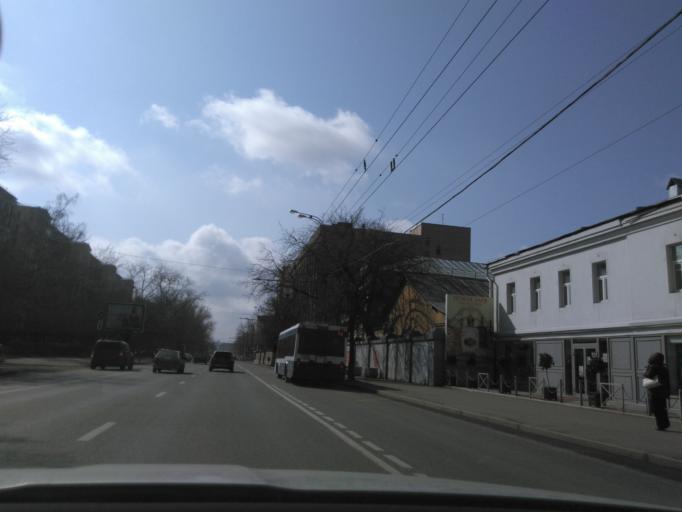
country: RU
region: Moscow
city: Zamoskvorech'ye
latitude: 55.7208
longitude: 37.6224
